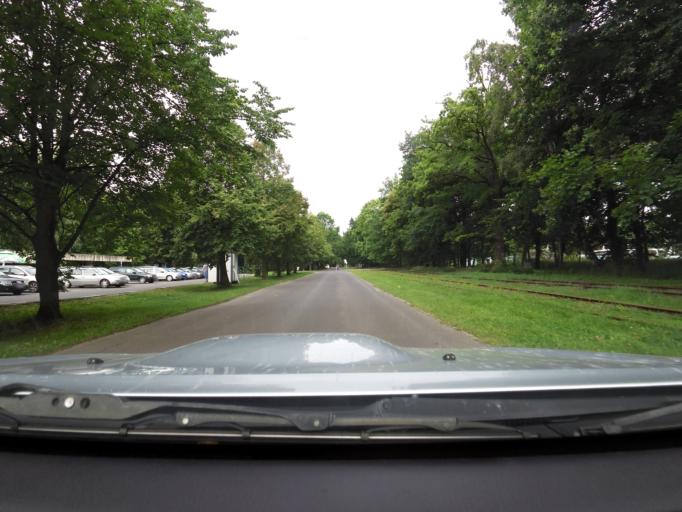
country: PL
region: Pomeranian Voivodeship
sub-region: Gdansk
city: Gdansk
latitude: 54.4060
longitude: 18.6779
